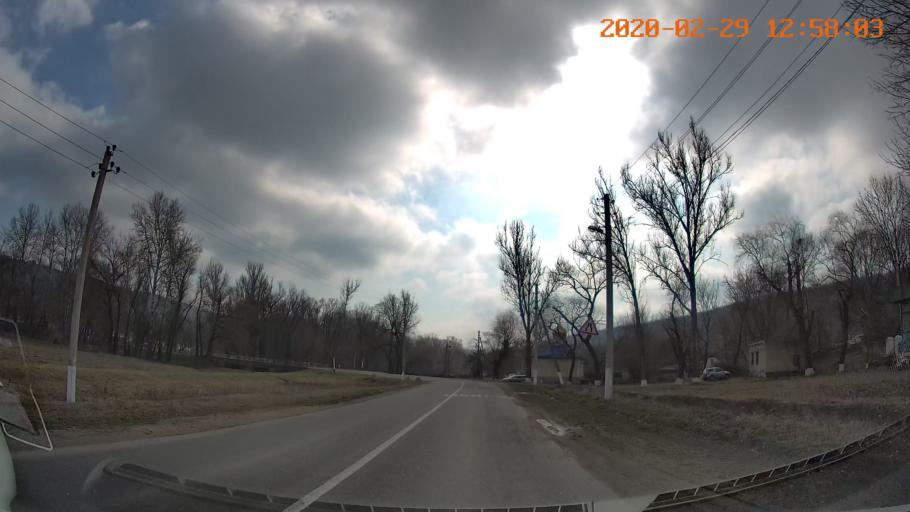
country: MD
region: Telenesti
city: Camenca
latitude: 48.0718
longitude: 28.7177
